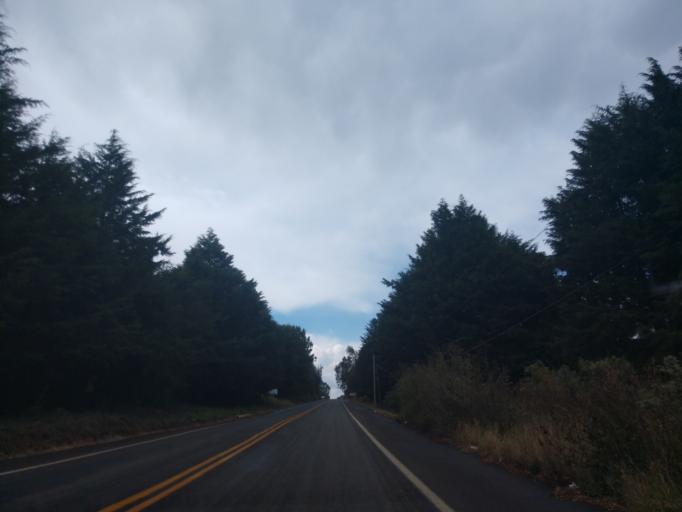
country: MX
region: Jalisco
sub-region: Mazamitla
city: Mazamitla
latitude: 19.9371
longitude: -103.0565
